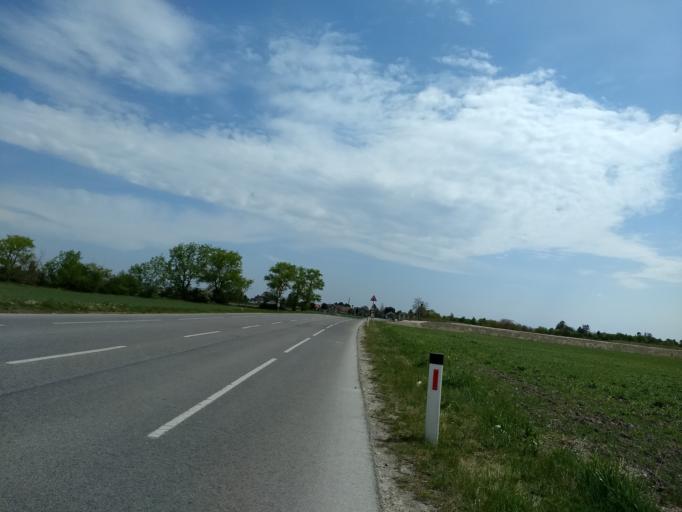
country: AT
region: Lower Austria
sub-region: Politischer Bezirk Ganserndorf
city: Gross-Enzersdorf
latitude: 48.2331
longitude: 16.5125
